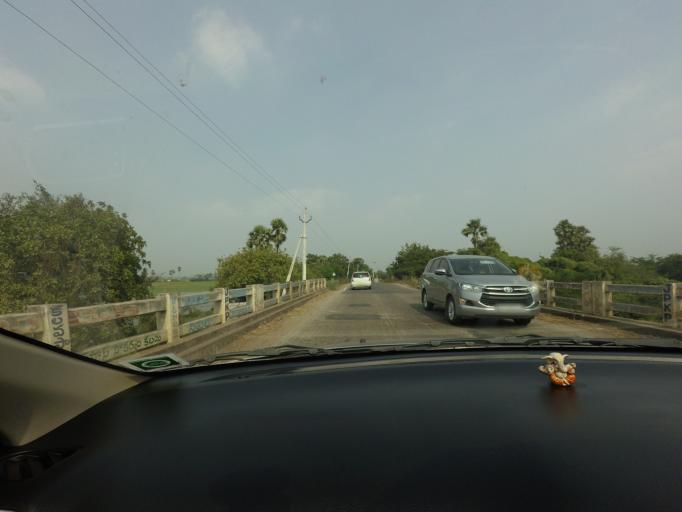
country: IN
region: Andhra Pradesh
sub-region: Krishna
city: Kankipadu
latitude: 16.4555
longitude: 80.7949
